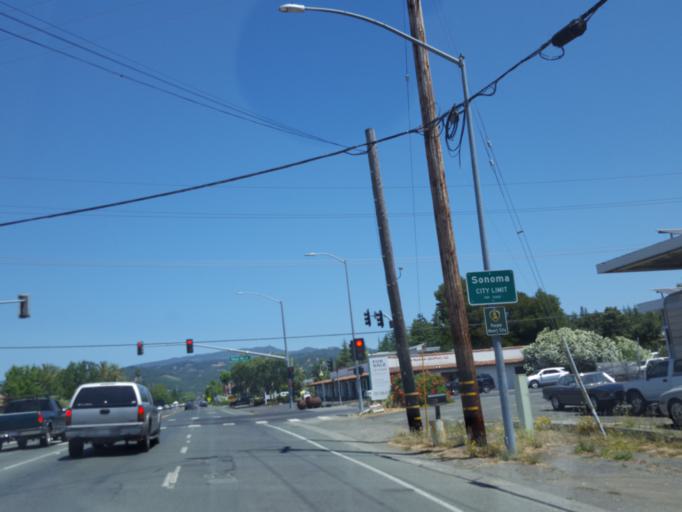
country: US
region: California
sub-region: Sonoma County
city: Sonoma
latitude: 38.2753
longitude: -122.4603
